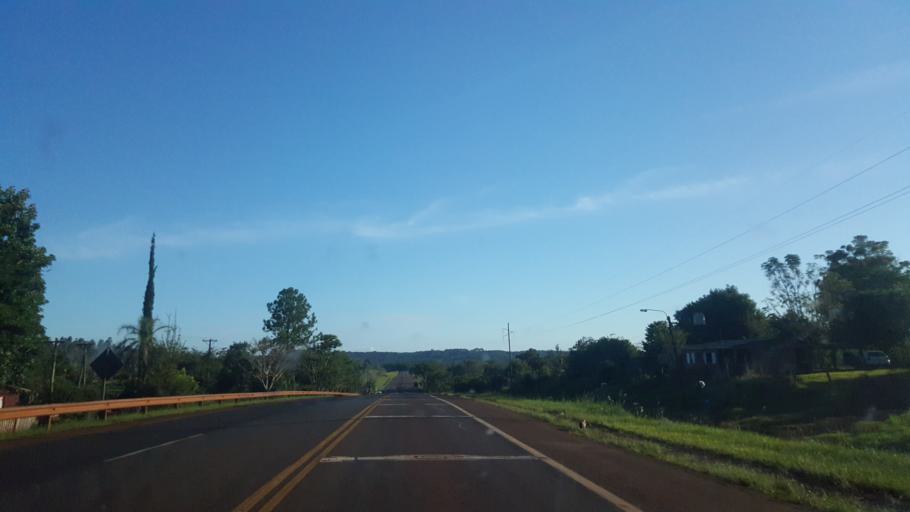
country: AR
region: Misiones
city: Caraguatay
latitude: -26.6387
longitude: -54.7521
